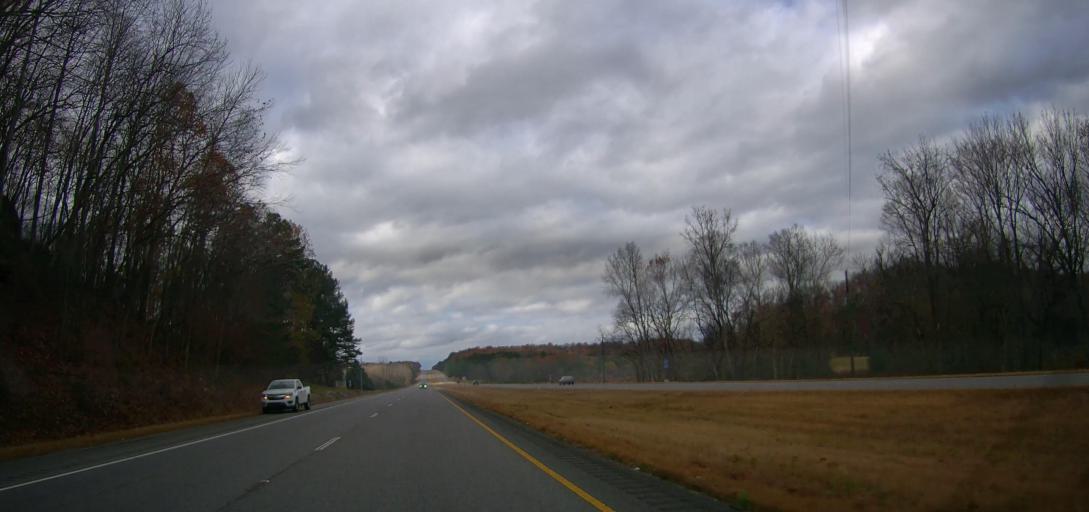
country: US
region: Alabama
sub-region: Lawrence County
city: Town Creek
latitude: 34.6086
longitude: -87.4542
